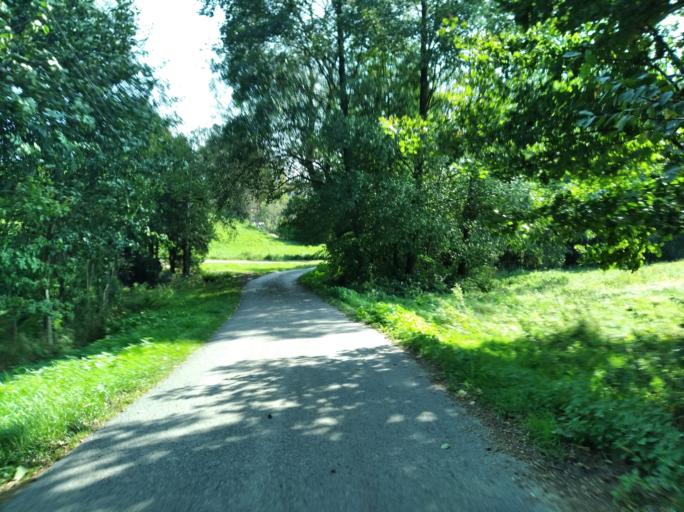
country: PL
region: Subcarpathian Voivodeship
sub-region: Powiat strzyzowski
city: Babica
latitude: 49.9384
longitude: 21.8600
